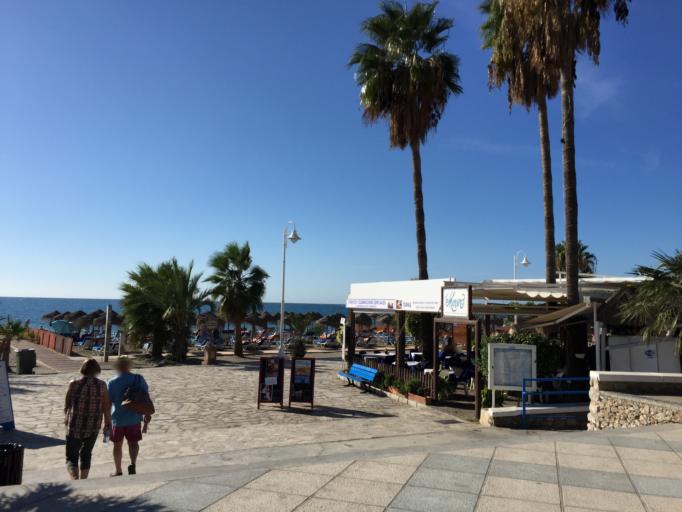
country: ES
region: Andalusia
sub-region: Provincia de Malaga
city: Nerja
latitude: 36.7499
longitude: -3.8689
